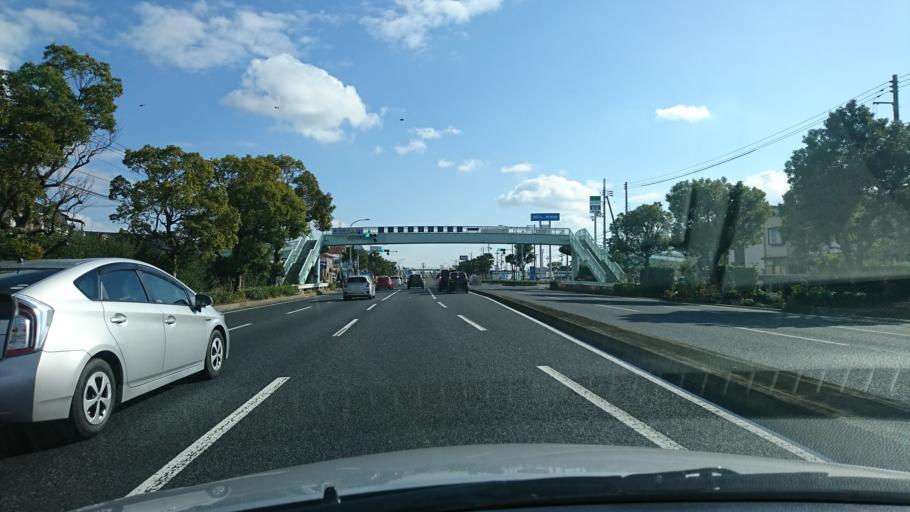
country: JP
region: Hyogo
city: Kakogawacho-honmachi
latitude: 34.7599
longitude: 134.8181
